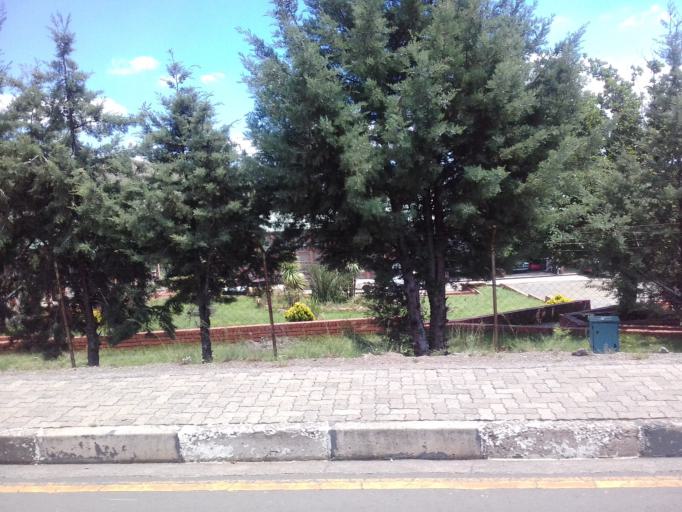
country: LS
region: Thaba-Tseka
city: Thaba-Tseka
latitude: -29.5209
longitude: 28.6084
